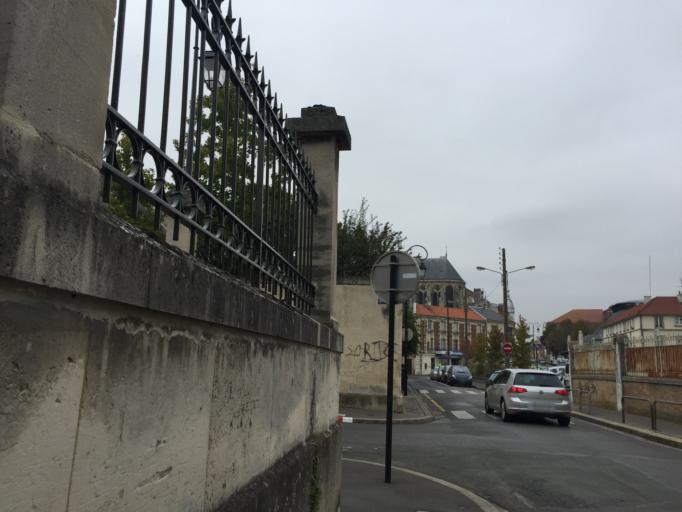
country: FR
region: Picardie
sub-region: Departement de l'Aisne
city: Soissons
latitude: 49.3788
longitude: 3.3266
